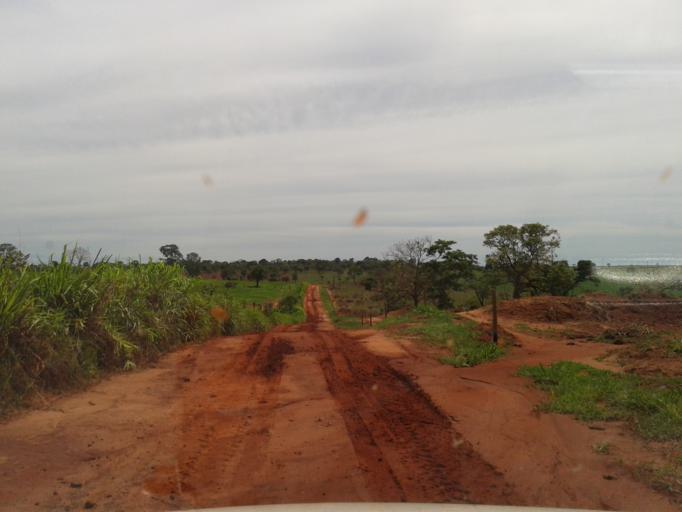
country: BR
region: Minas Gerais
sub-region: Santa Vitoria
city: Santa Vitoria
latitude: -19.2119
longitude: -50.6540
